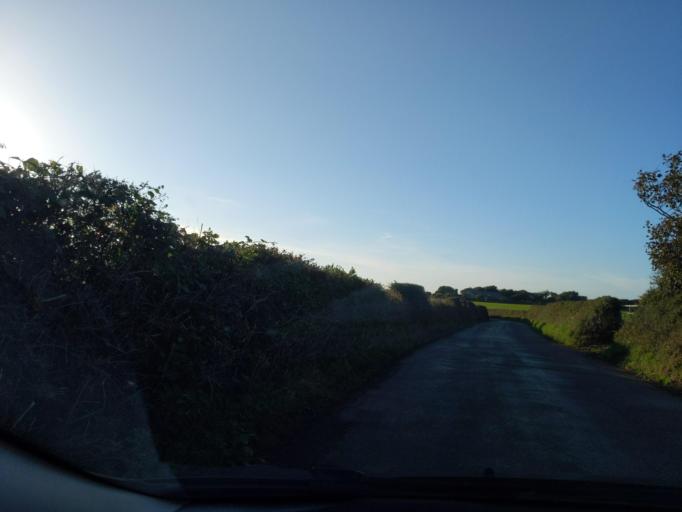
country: GB
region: England
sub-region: Plymouth
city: Plymstock
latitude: 50.3444
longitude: -4.1004
